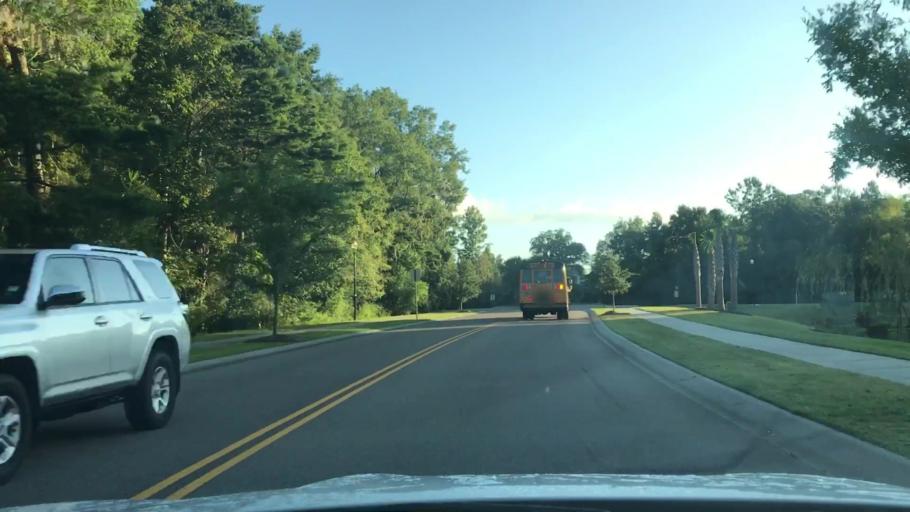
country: US
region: South Carolina
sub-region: Charleston County
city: Shell Point
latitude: 32.8304
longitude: -80.0967
